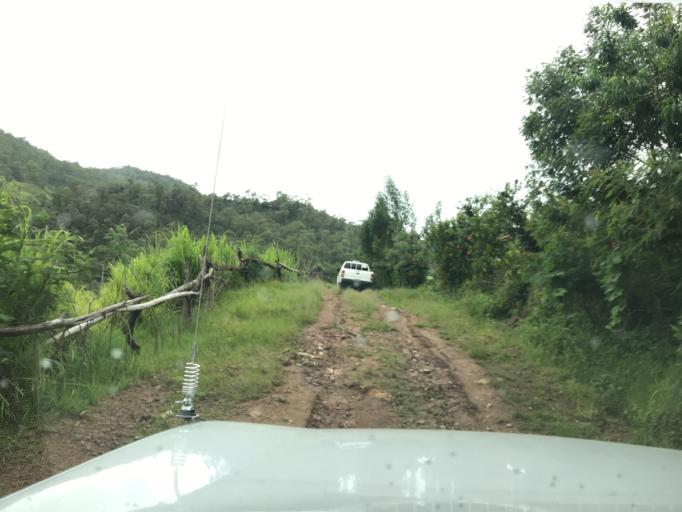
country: TL
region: Ainaro
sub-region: Ainaro
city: Ainaro
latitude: -8.8679
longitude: 125.5521
